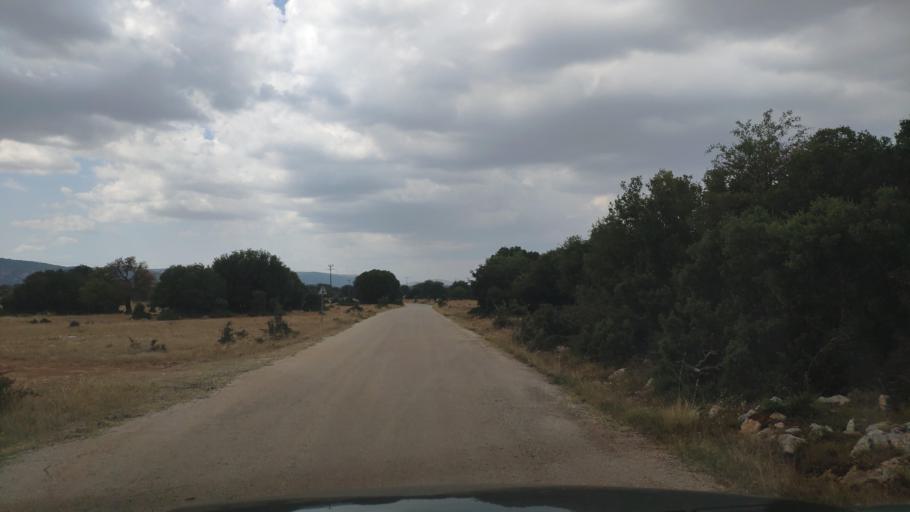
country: GR
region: Peloponnese
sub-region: Nomos Lakonias
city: Kariai
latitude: 37.3095
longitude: 22.4532
